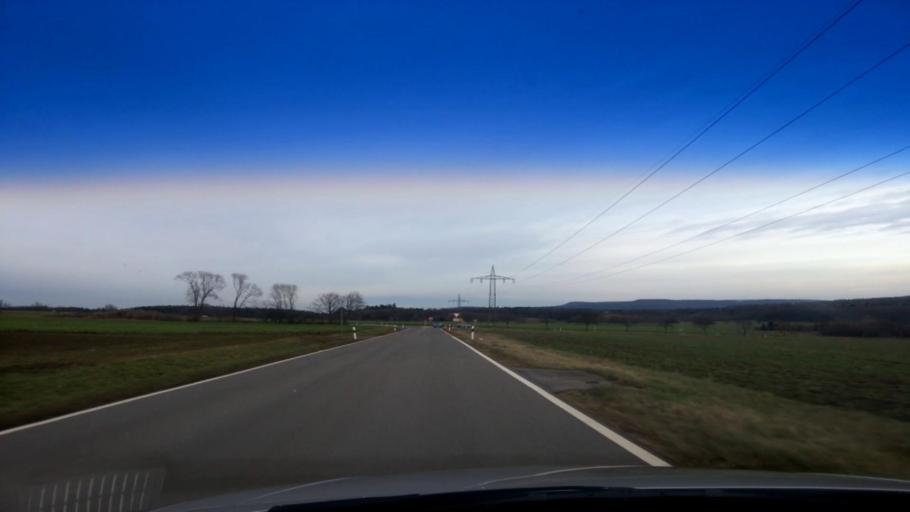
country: DE
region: Bavaria
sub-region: Upper Franconia
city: Litzendorf
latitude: 49.8794
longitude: 11.0062
